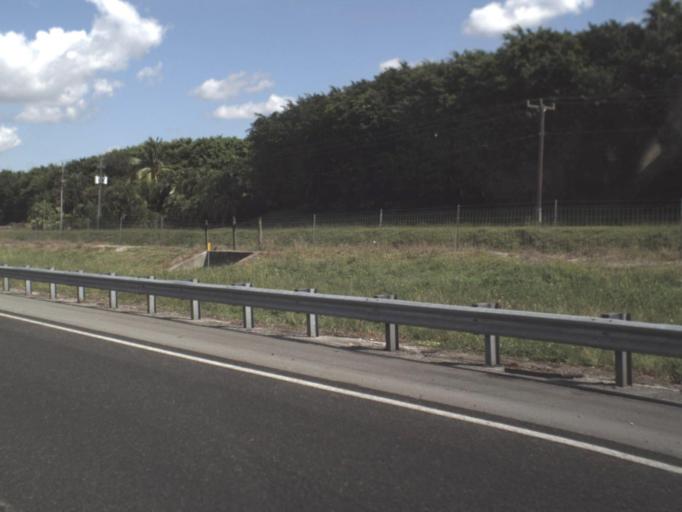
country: US
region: Florida
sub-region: Palm Beach County
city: Boca Del Mar
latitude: 26.3782
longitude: -80.1708
